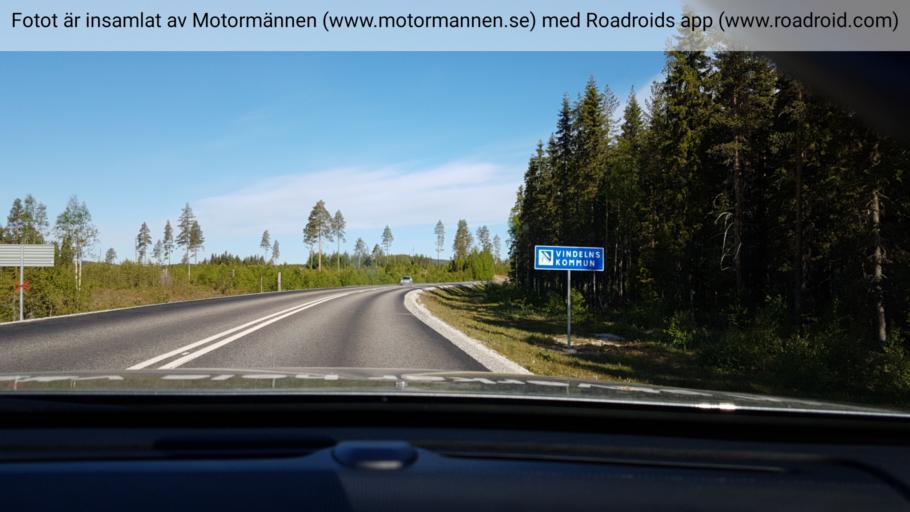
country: SE
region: Vaesterbotten
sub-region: Vindelns Kommun
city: Vindeln
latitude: 64.0549
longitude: 19.6539
